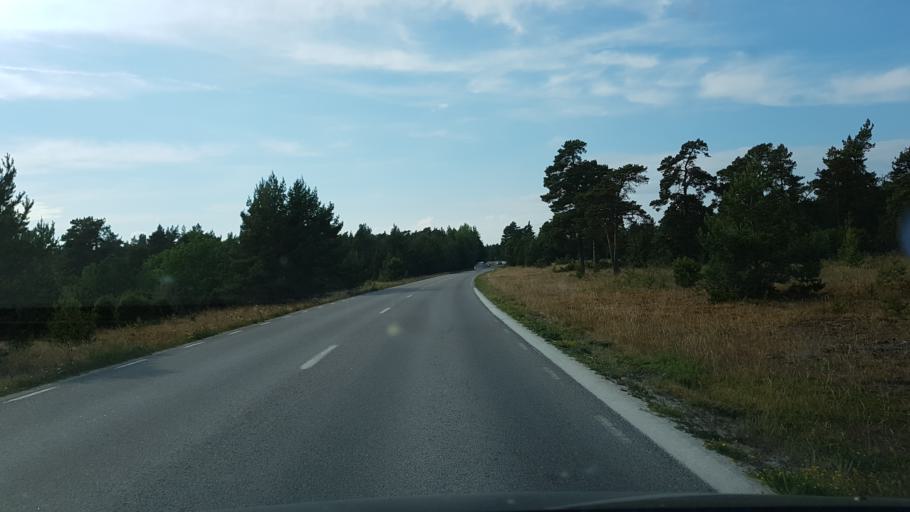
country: SE
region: Gotland
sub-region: Gotland
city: Visby
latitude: 57.6338
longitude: 18.4078
